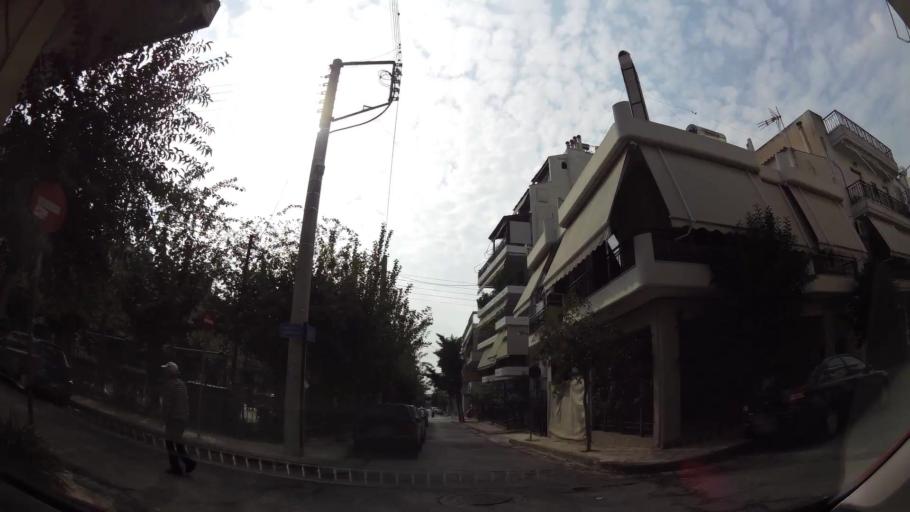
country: GR
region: Attica
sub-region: Nomarchia Athinas
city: Ilion
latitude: 38.0298
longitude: 23.6882
